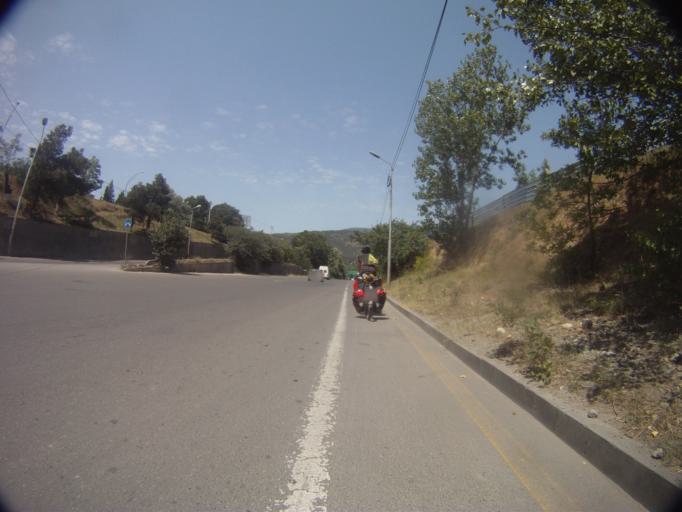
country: GE
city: Zahesi
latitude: 41.8186
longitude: 44.7716
